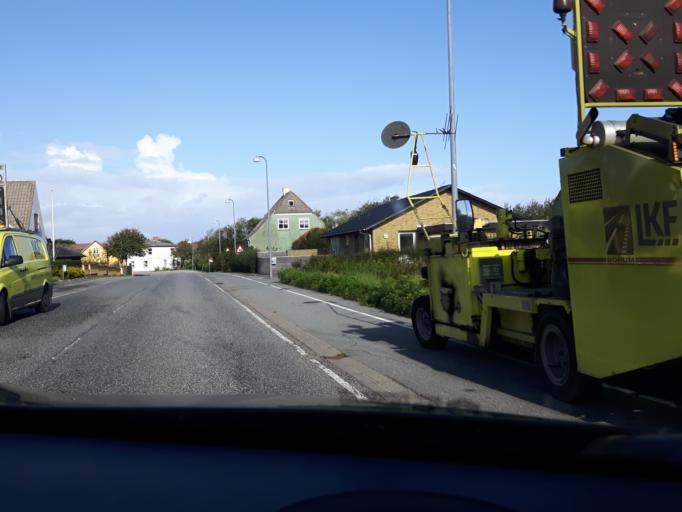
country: DK
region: North Denmark
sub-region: Hjorring Kommune
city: Hjorring
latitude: 57.4671
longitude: 9.8068
